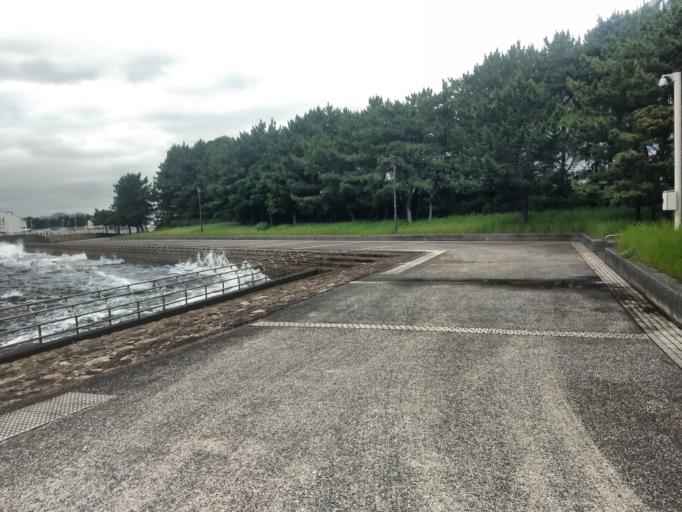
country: JP
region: Kanagawa
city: Yokosuka
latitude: 35.3377
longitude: 139.6487
